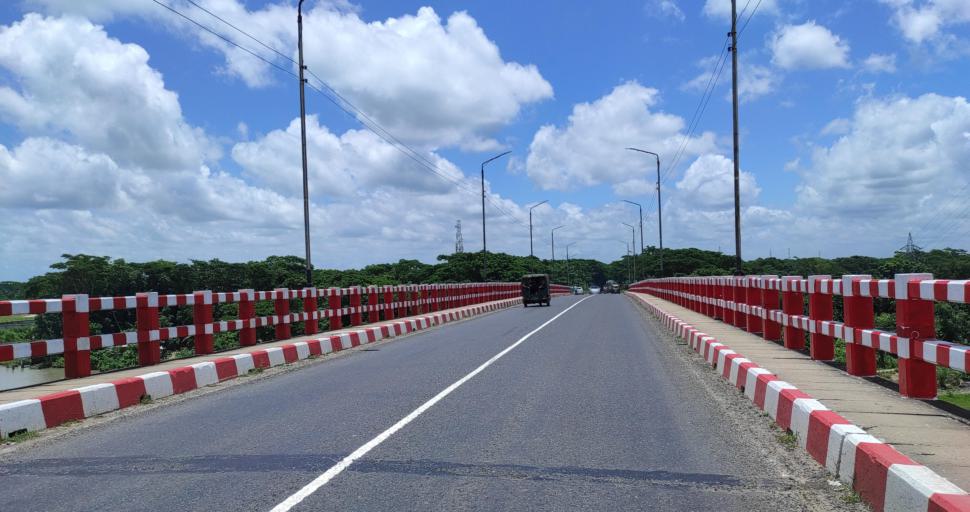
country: BD
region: Barisal
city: Gaurnadi
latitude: 22.8241
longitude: 90.2638
